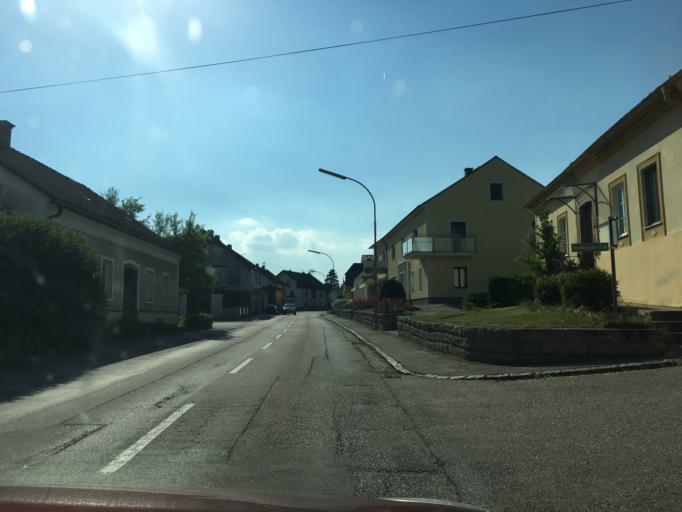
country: AT
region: Lower Austria
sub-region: Politischer Bezirk Amstetten
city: Ennsdorf
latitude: 48.2718
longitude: 14.5260
